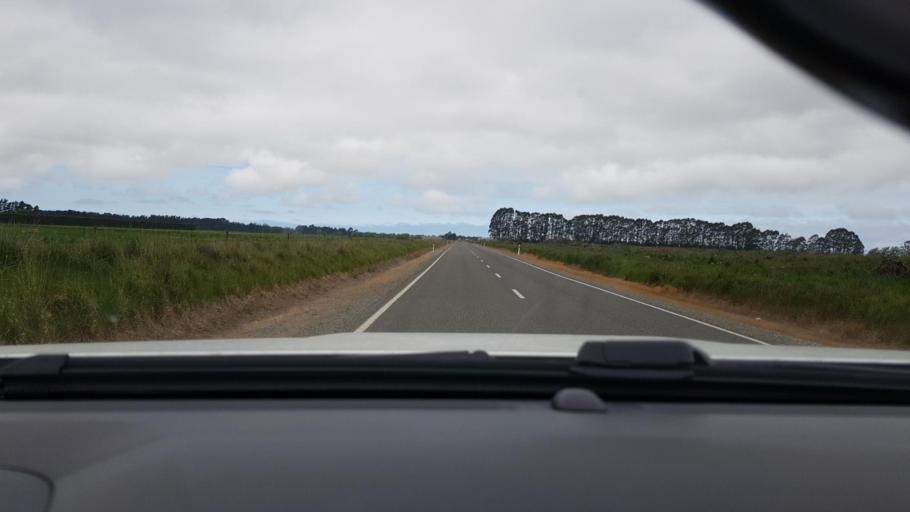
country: NZ
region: Otago
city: Oamaru
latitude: -44.9645
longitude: 171.0509
